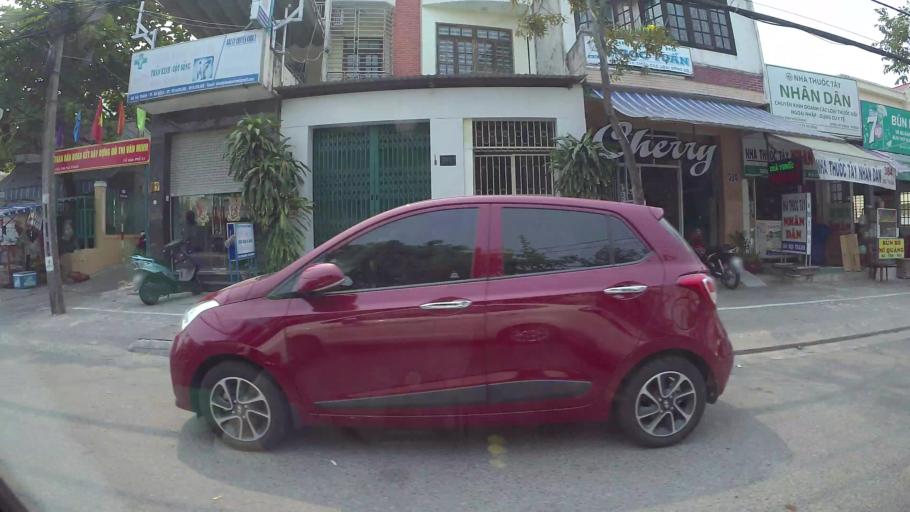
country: VN
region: Da Nang
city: Son Tra
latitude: 16.0389
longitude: 108.2219
